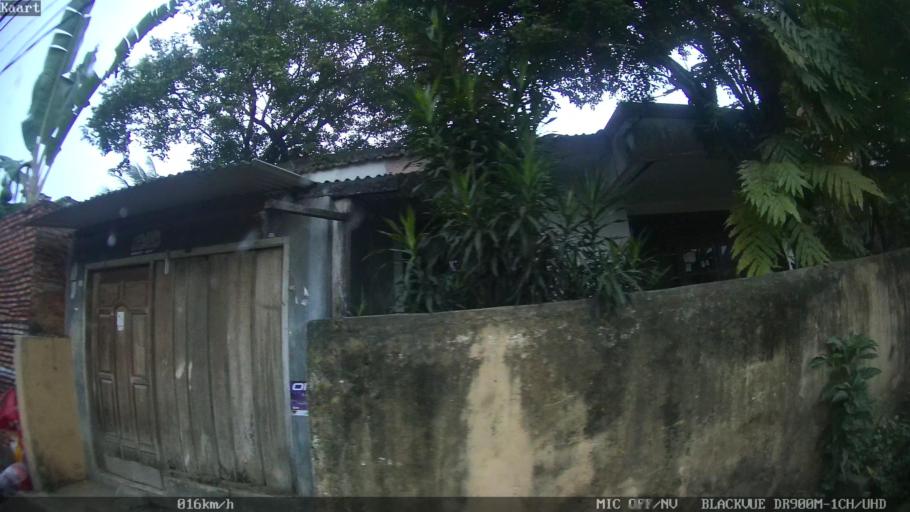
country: ID
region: Lampung
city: Kedaton
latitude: -5.3988
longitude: 105.2716
